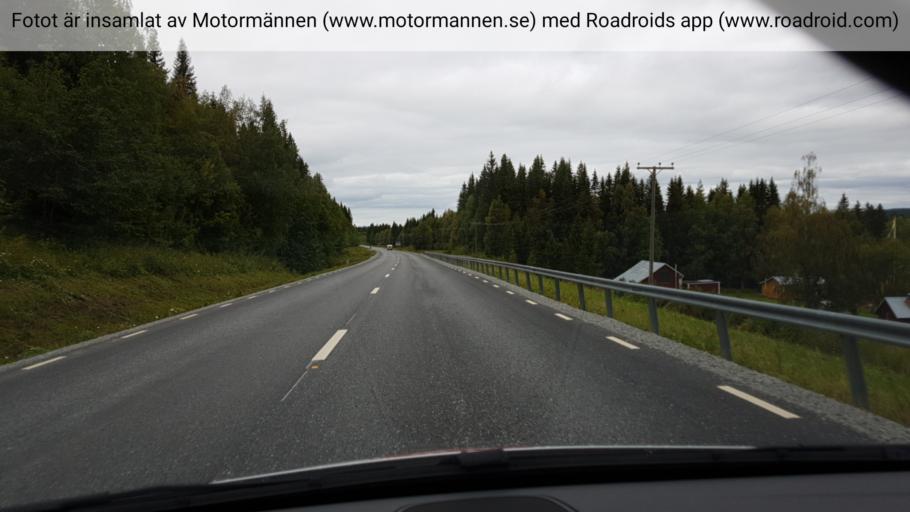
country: SE
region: Jaemtland
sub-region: Stroemsunds Kommun
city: Stroemsund
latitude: 64.2203
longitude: 15.5429
